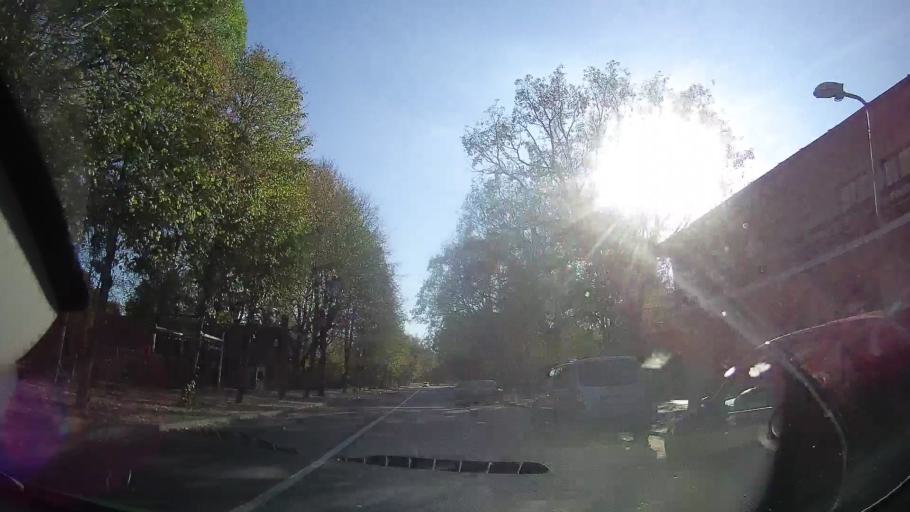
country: RO
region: Constanta
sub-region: Comuna Douazeci si Trei August
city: Douazeci si Trei August
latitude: 43.8768
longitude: 28.6030
